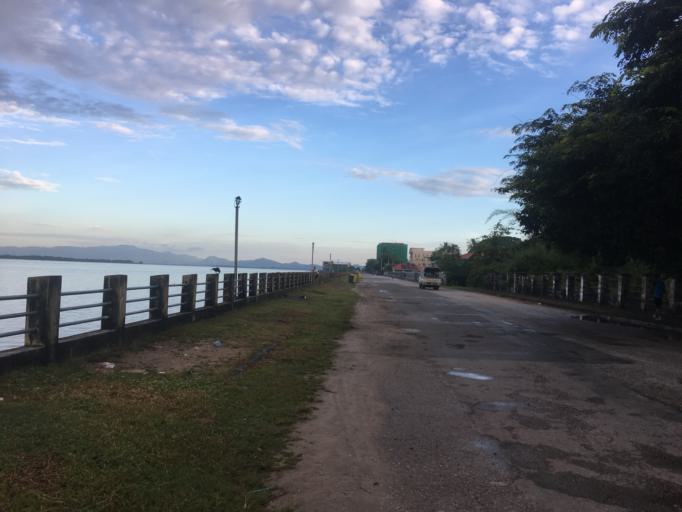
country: MM
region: Mon
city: Mawlamyine
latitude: 16.4664
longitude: 97.6221
